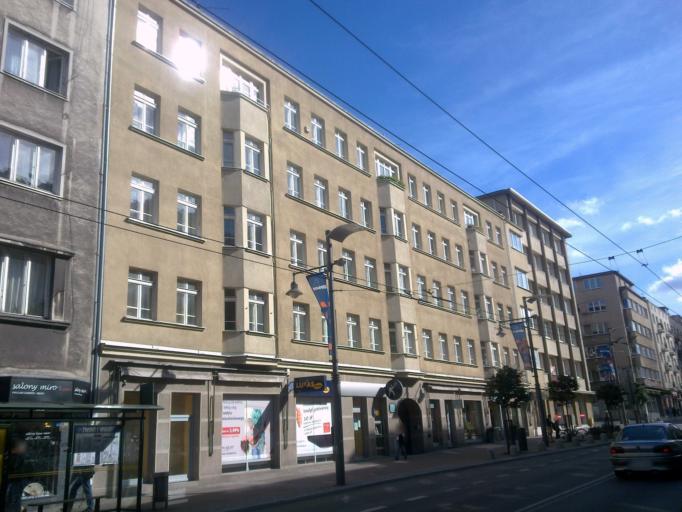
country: PL
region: Pomeranian Voivodeship
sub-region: Gdynia
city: Gdynia
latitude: 54.5155
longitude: 18.5406
